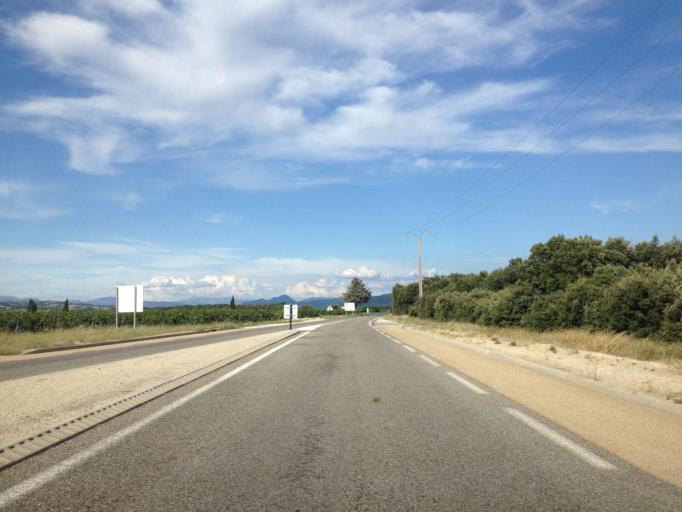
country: FR
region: Provence-Alpes-Cote d'Azur
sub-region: Departement du Vaucluse
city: Violes
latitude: 44.1846
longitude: 4.9545
